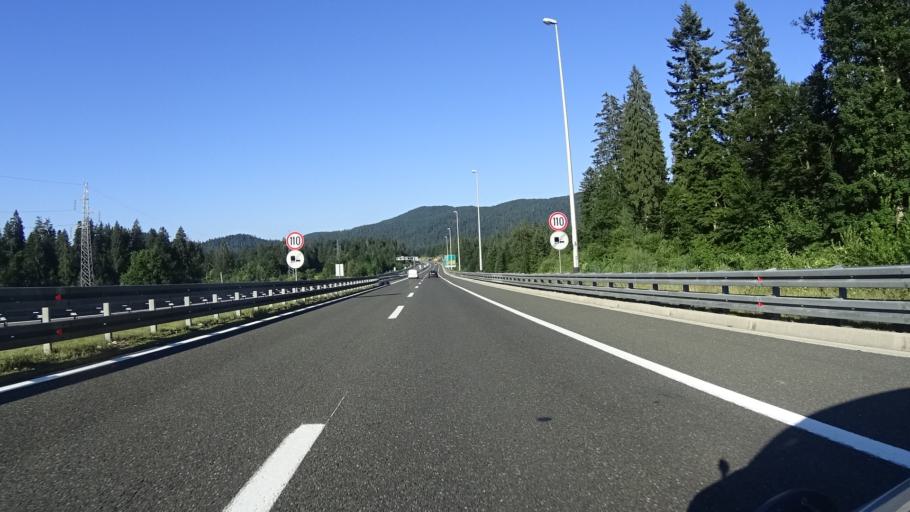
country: HR
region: Primorsko-Goranska
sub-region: Grad Delnice
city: Delnice
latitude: 45.3690
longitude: 14.7768
